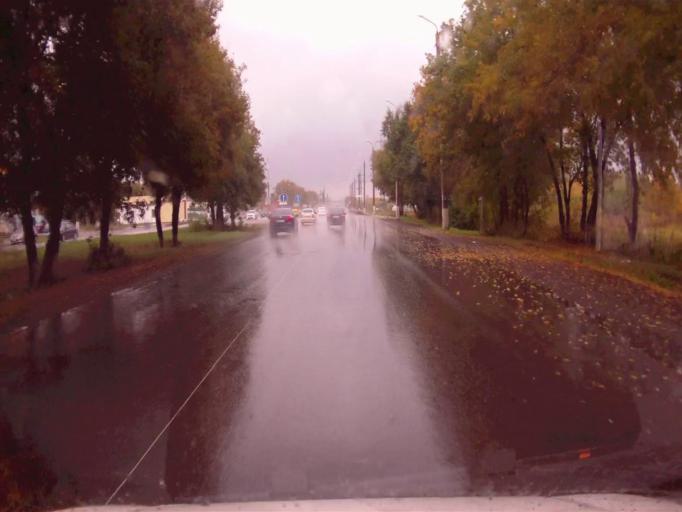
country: RU
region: Chelyabinsk
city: Dolgoderevenskoye
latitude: 55.2522
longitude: 61.3549
